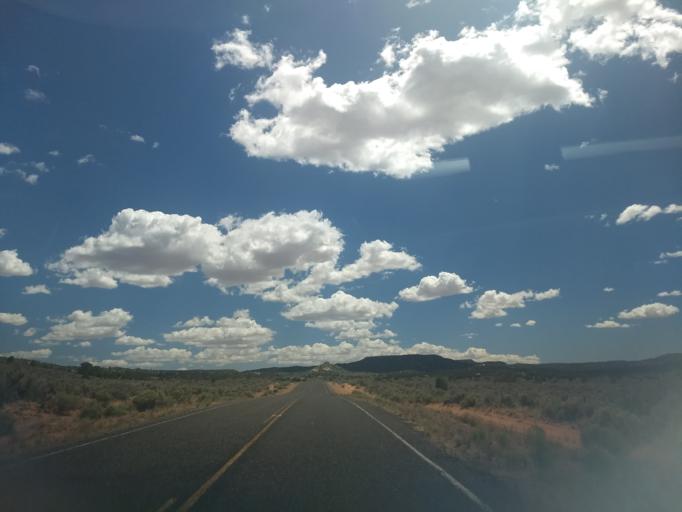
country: US
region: Utah
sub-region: Kane County
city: Kanab
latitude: 37.1596
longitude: -112.6676
